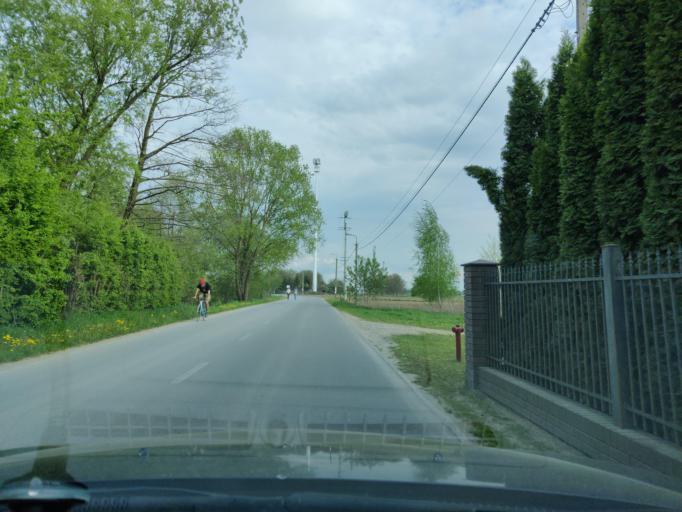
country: PL
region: Masovian Voivodeship
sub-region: Powiat piaseczynski
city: Konstancin-Jeziorna
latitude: 52.1273
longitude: 21.1391
